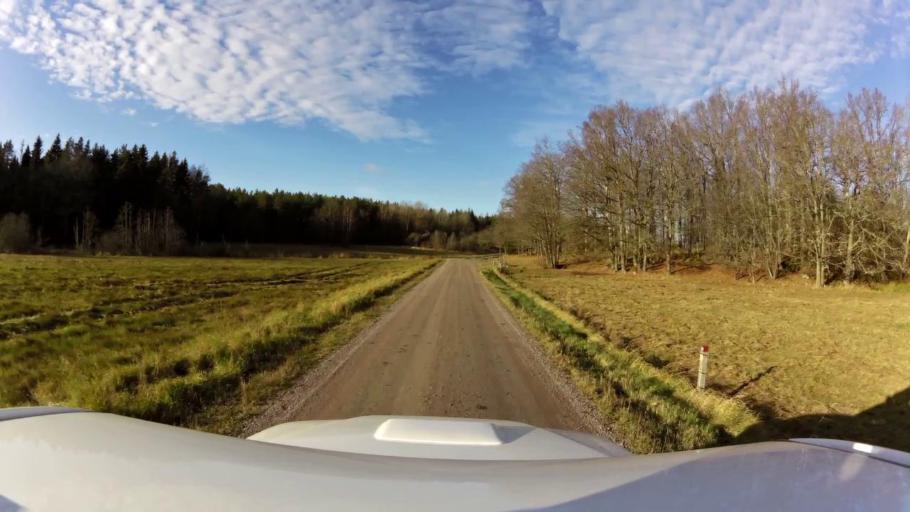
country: SE
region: OEstergoetland
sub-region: Linkopings Kommun
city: Linkoping
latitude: 58.3575
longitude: 15.6067
